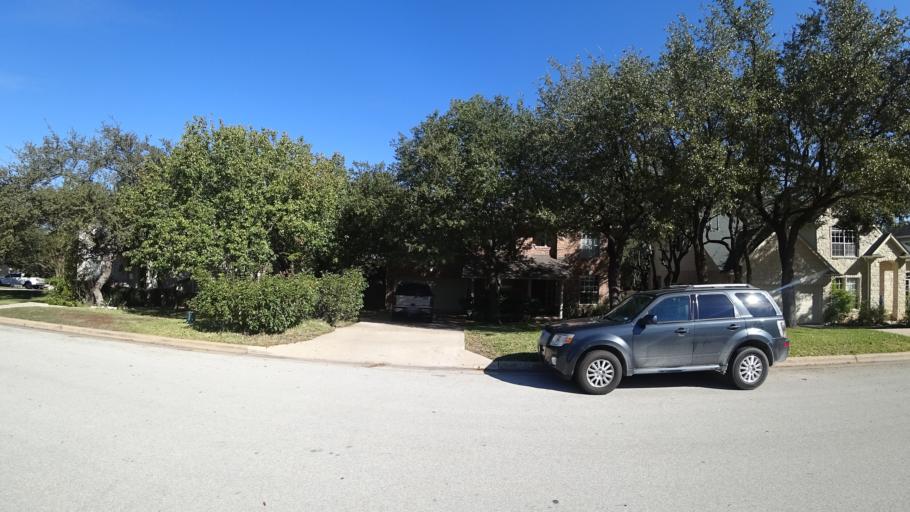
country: US
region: Texas
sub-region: Travis County
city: Hudson Bend
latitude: 30.3767
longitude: -97.8954
